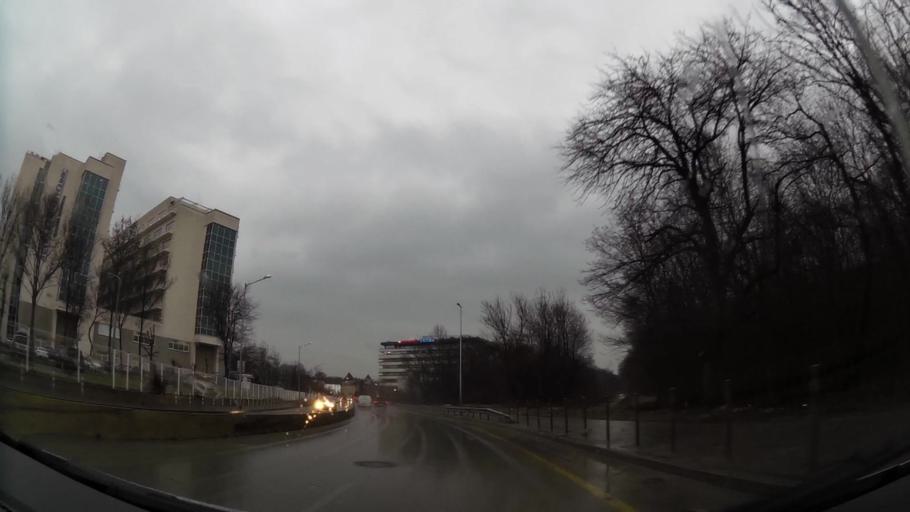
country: BG
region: Sofia-Capital
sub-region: Stolichna Obshtina
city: Sofia
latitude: 42.6636
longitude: 23.3251
